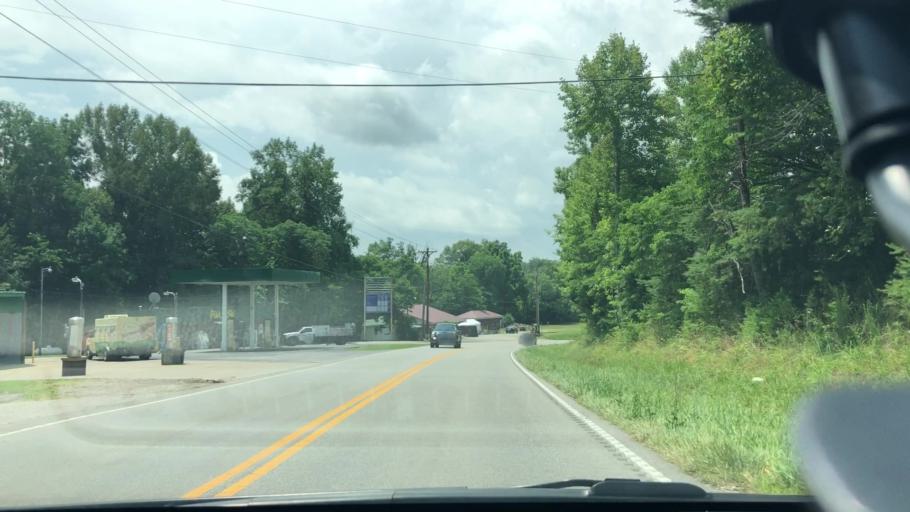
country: US
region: Kentucky
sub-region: Pulaski County
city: Somerset
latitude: 37.0551
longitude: -84.6765
